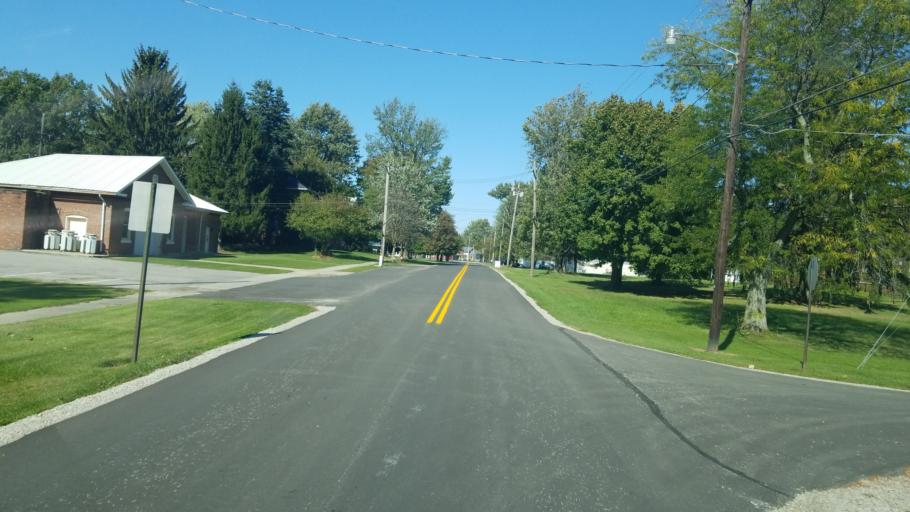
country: US
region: Ohio
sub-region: Huron County
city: Greenwich
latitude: 41.0266
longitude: -82.5193
